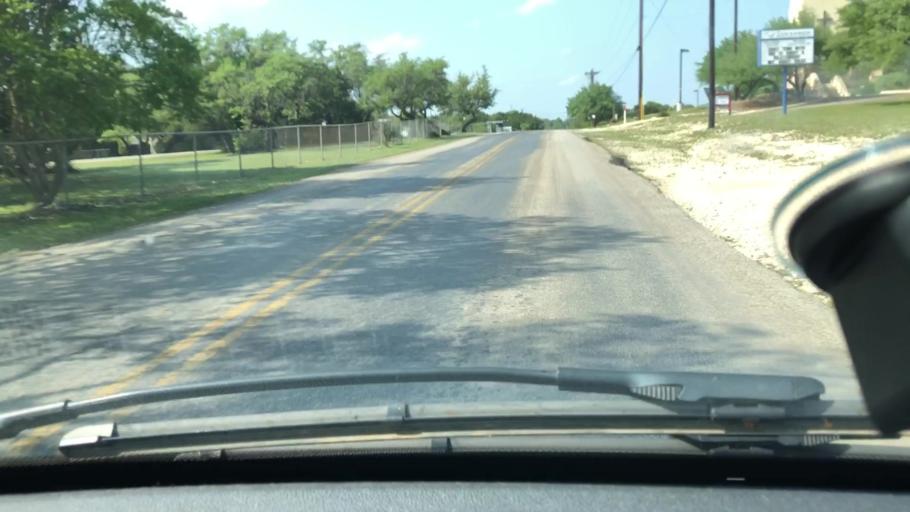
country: US
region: Texas
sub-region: Comal County
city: Bulverde
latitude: 29.7677
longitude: -98.4588
